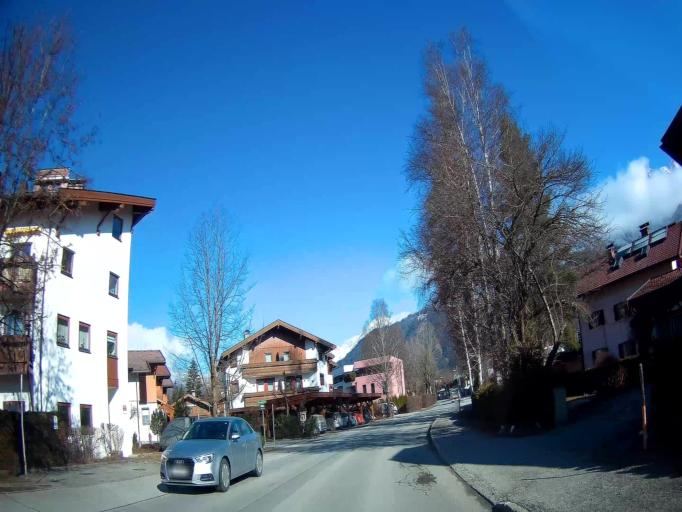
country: AT
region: Salzburg
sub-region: Politischer Bezirk Zell am See
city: Saalfelden am Steinernen Meer
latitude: 47.4296
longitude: 12.8522
